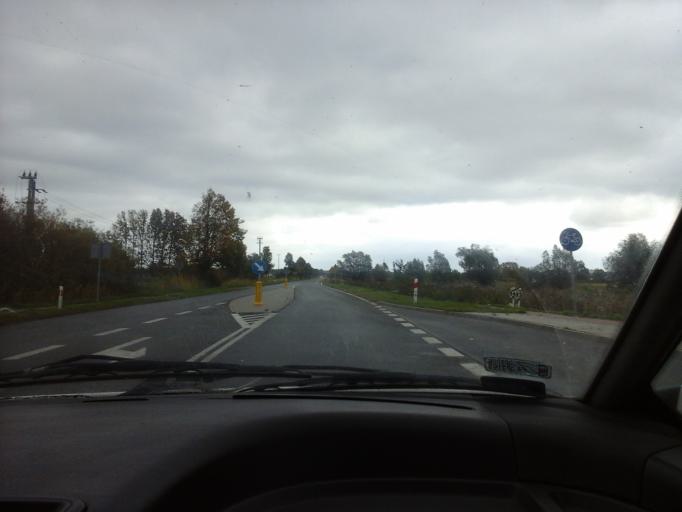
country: PL
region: Pomeranian Voivodeship
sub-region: Powiat gdanski
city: Cedry Wielkie
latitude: 54.3306
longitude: 18.8020
